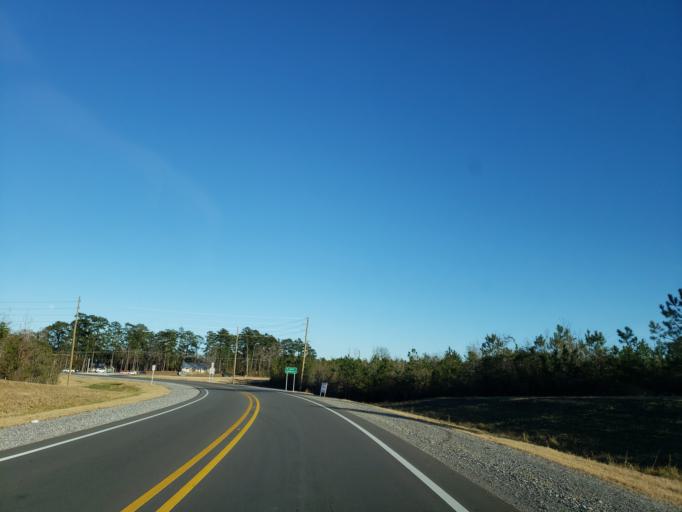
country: US
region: Mississippi
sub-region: Forrest County
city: Rawls Springs
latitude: 31.4187
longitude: -89.4123
